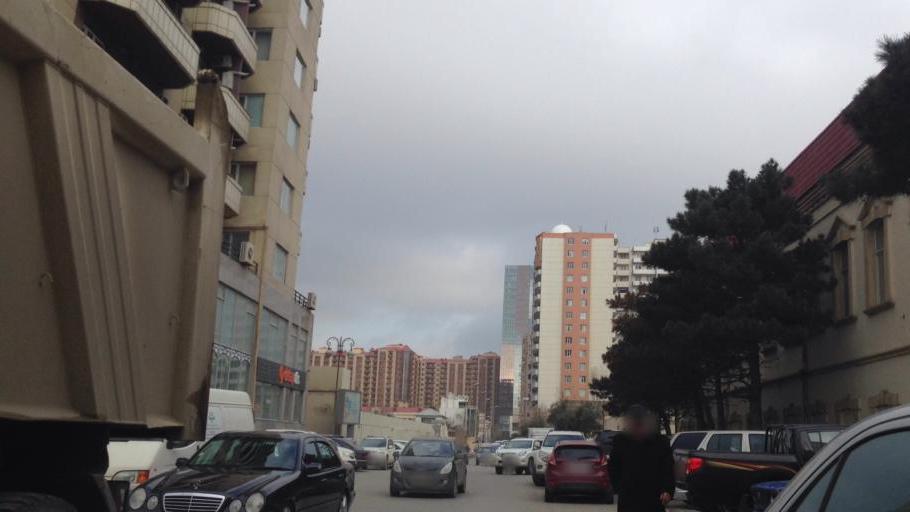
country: AZ
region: Baki
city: Baku
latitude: 40.3780
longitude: 49.8724
